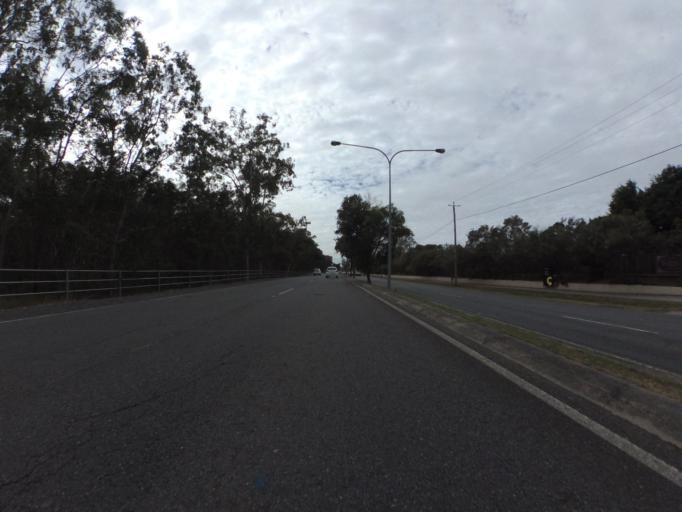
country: AU
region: Queensland
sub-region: Brisbane
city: Wynnum West
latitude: -27.4654
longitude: 153.1422
